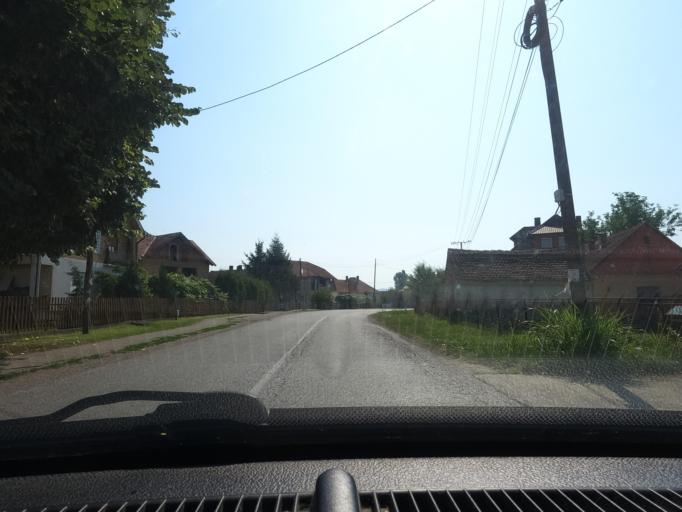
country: RS
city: Lipnicki Sor
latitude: 44.5825
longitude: 19.2569
